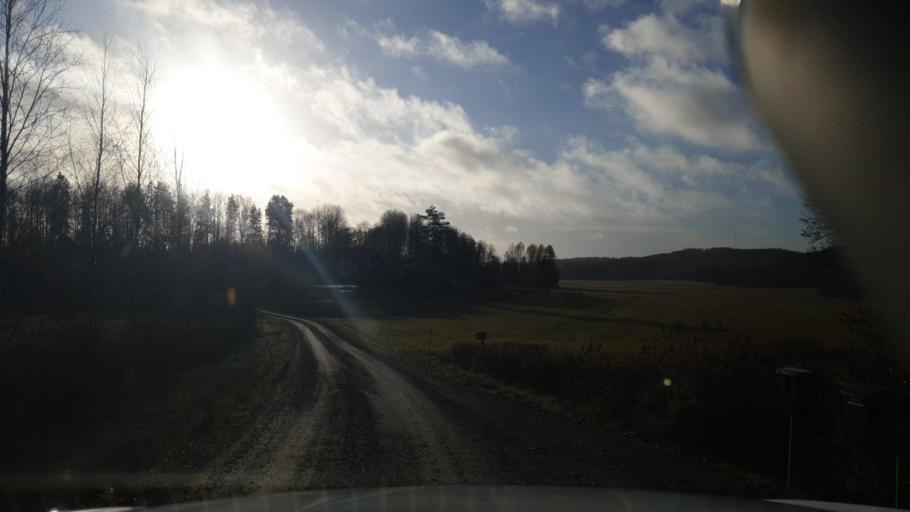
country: SE
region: Vaermland
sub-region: Grums Kommun
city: Grums
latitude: 59.4924
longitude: 12.9266
